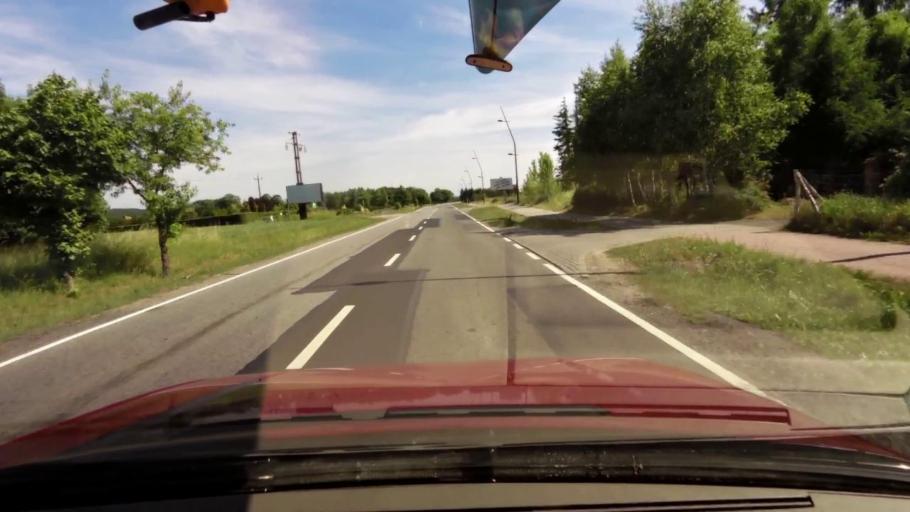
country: PL
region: Pomeranian Voivodeship
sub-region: Powiat slupski
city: Kobylnica
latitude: 54.4319
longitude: 17.0029
